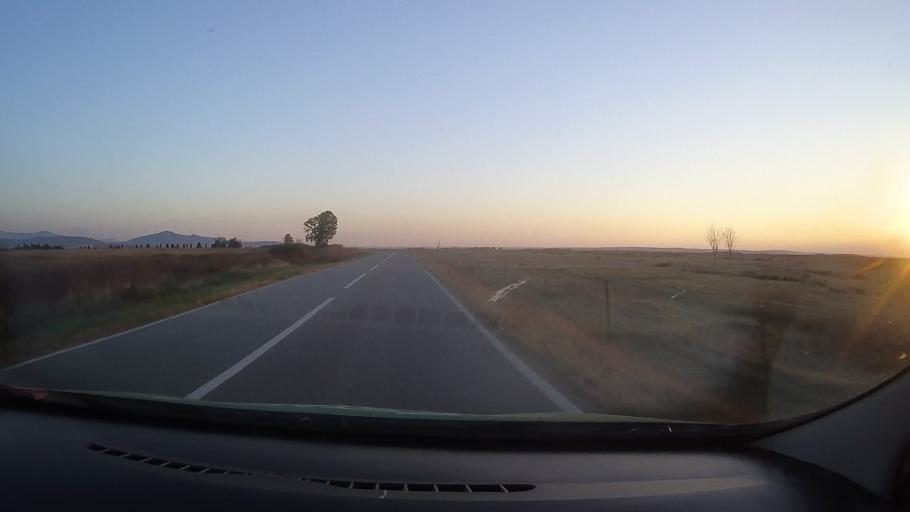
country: RO
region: Timis
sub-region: Comuna Manastiur
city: Manastiur
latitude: 45.8216
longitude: 22.0706
